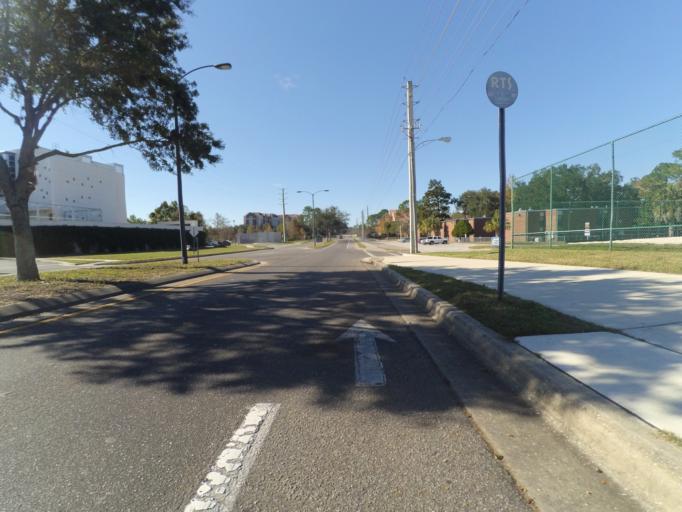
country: US
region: Florida
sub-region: Alachua County
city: Gainesville
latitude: 29.6377
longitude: -82.3701
